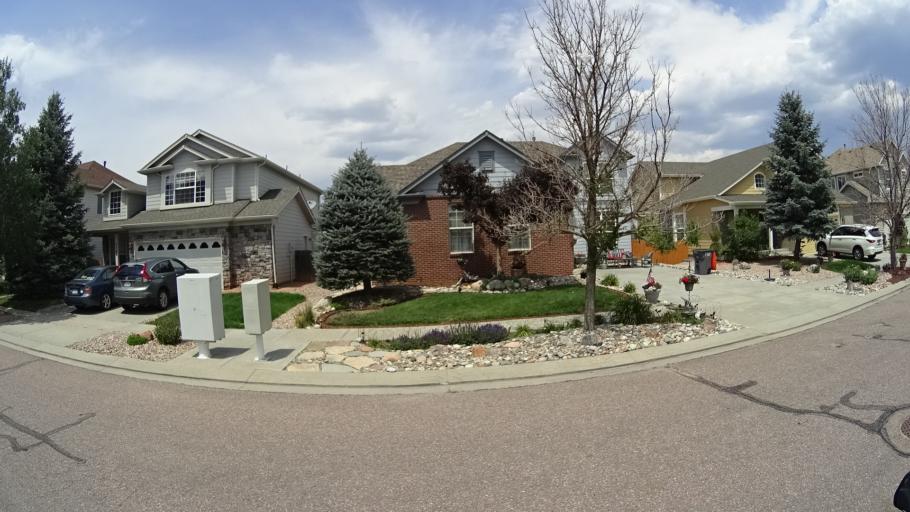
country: US
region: Colorado
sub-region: El Paso County
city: Black Forest
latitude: 38.9620
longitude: -104.7615
